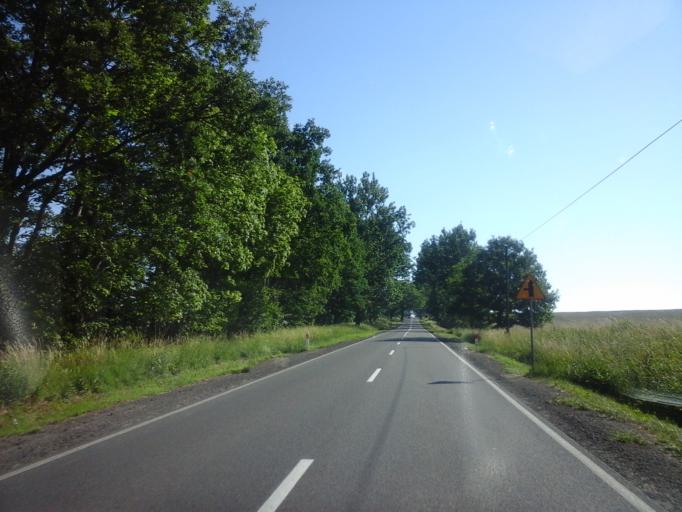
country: PL
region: West Pomeranian Voivodeship
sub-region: Powiat drawski
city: Drawsko Pomorskie
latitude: 53.5125
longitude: 15.7672
